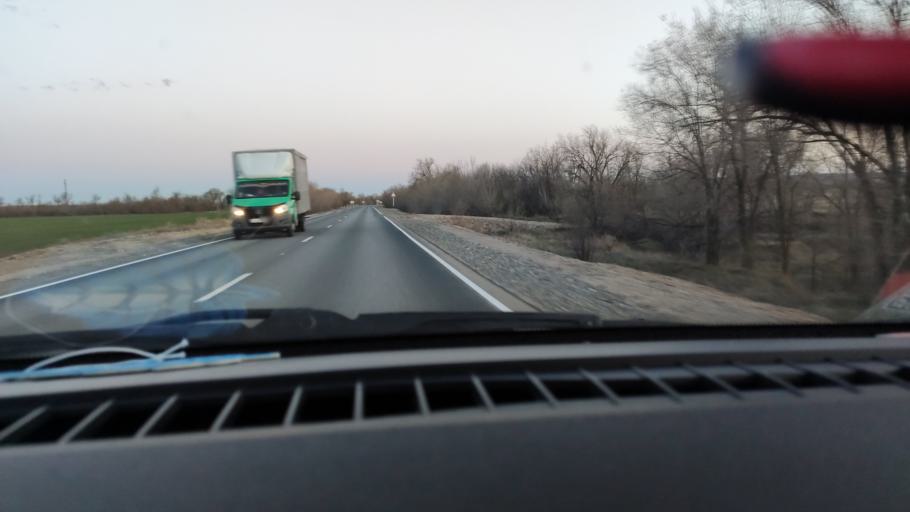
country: RU
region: Saratov
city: Krasnoarmeysk
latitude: 51.1110
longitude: 45.9581
